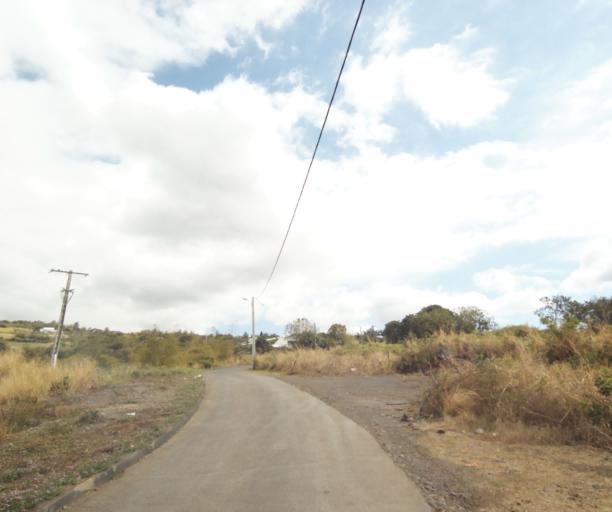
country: RE
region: Reunion
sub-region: Reunion
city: Saint-Paul
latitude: -21.0249
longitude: 55.2932
